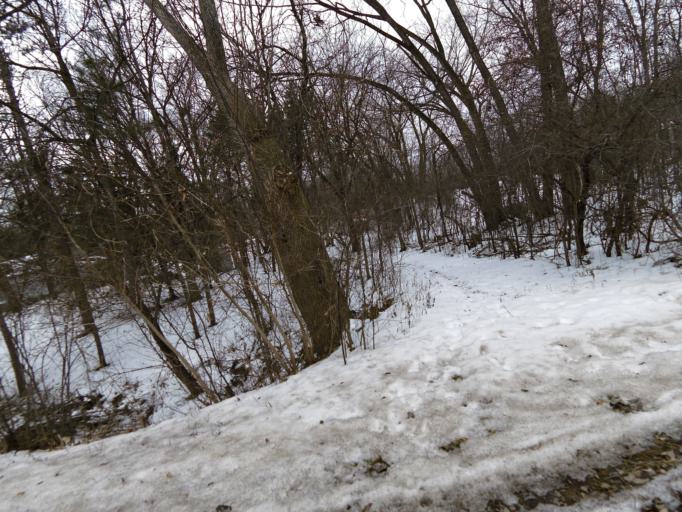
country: US
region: Minnesota
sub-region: Washington County
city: Lake Elmo
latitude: 44.9626
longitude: -92.8429
